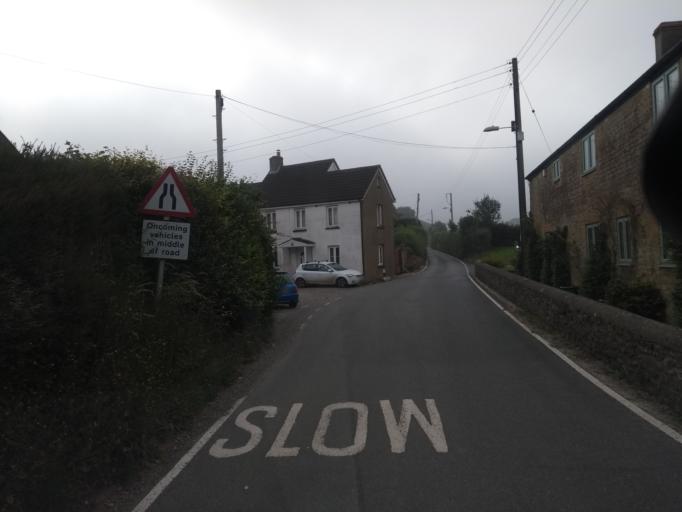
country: GB
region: England
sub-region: Somerset
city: Crewkerne
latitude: 50.8418
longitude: -2.8258
